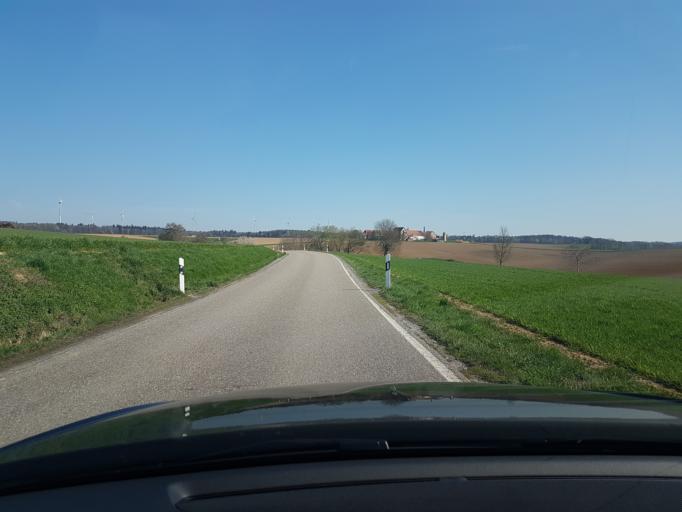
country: DE
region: Baden-Wuerttemberg
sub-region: Regierungsbezirk Stuttgart
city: Widdern
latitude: 49.2576
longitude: 9.4127
